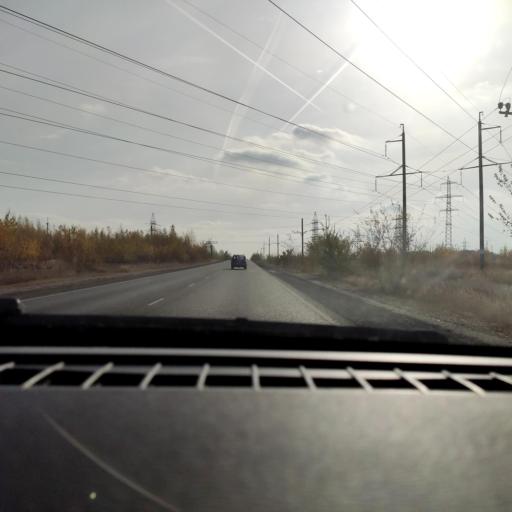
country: RU
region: Voronezj
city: Maslovka
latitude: 51.5828
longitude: 39.2597
